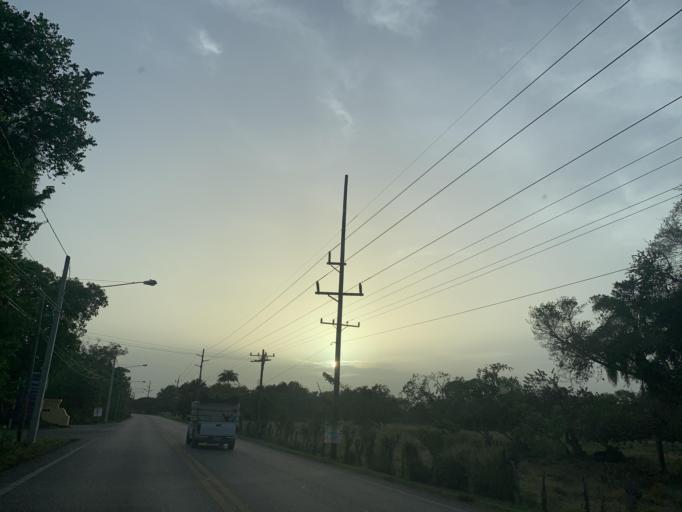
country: DO
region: Puerto Plata
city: Cabarete
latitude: 19.7787
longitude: -70.4788
